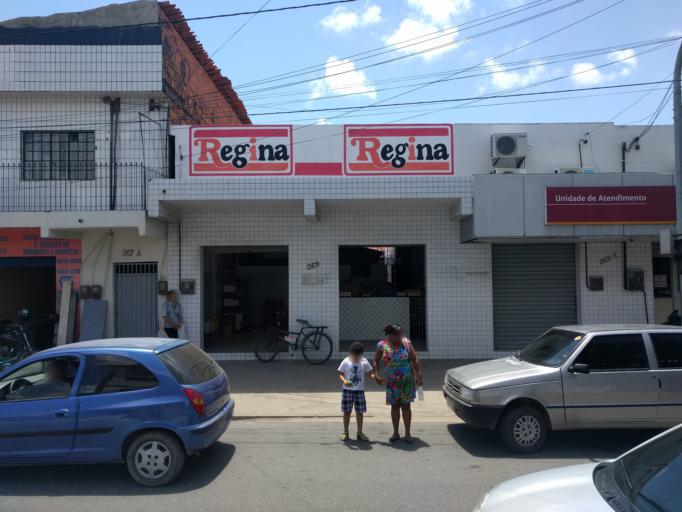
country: BR
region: Ceara
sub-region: Caucaia
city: Caucaia
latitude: -3.7649
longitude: -38.6527
